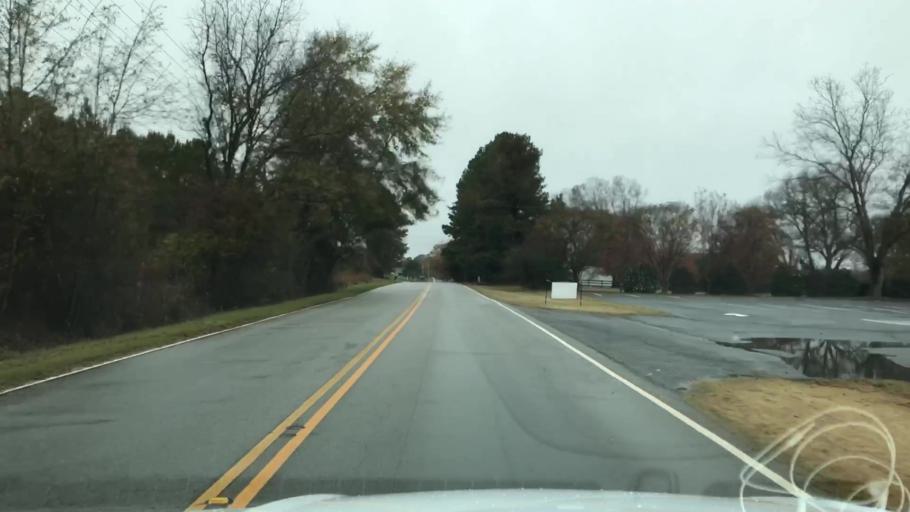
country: US
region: South Carolina
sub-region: Spartanburg County
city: Roebuck
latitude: 34.8042
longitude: -81.9172
